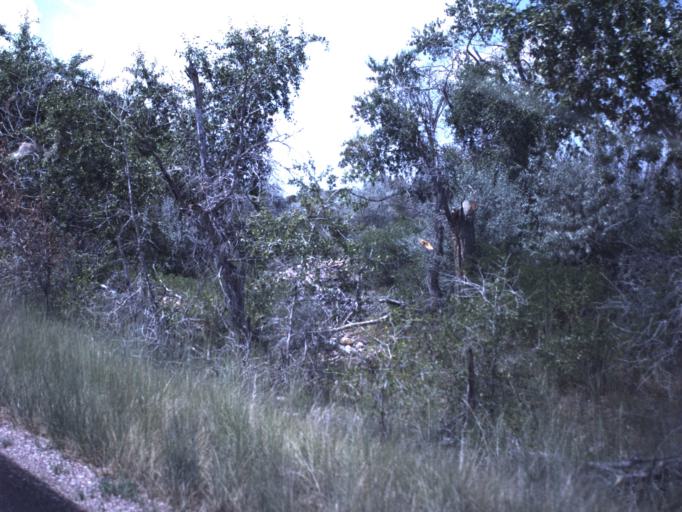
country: US
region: Utah
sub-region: Duchesne County
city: Roosevelt
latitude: 40.4038
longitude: -109.8819
